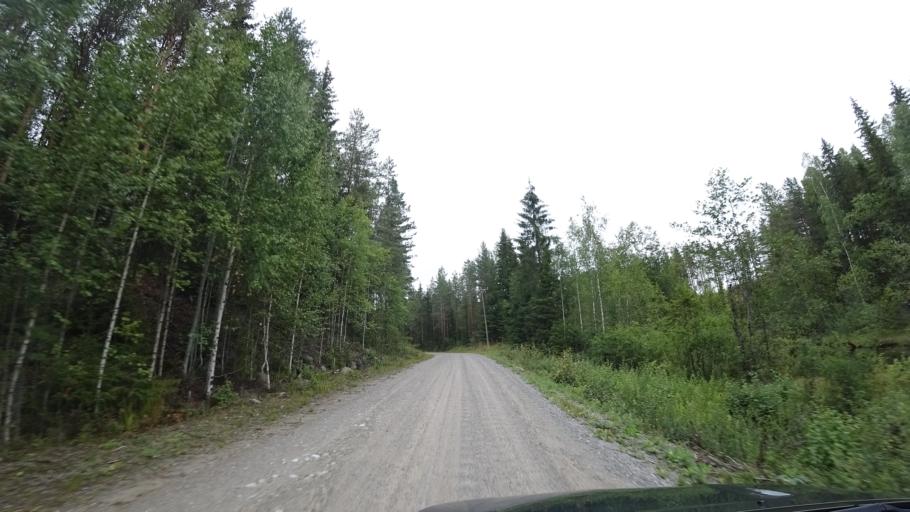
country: FI
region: Paijanne Tavastia
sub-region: Lahti
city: Auttoinen
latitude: 61.2175
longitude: 25.1369
